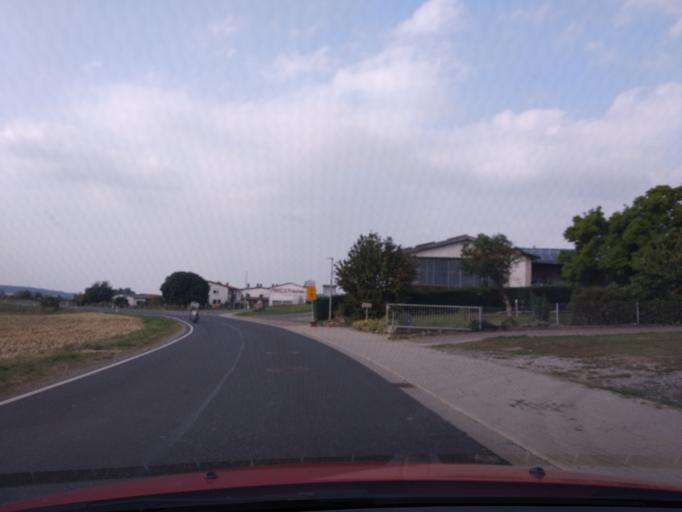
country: DE
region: Hesse
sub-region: Regierungsbezirk Kassel
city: Calden
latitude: 51.3882
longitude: 9.3646
